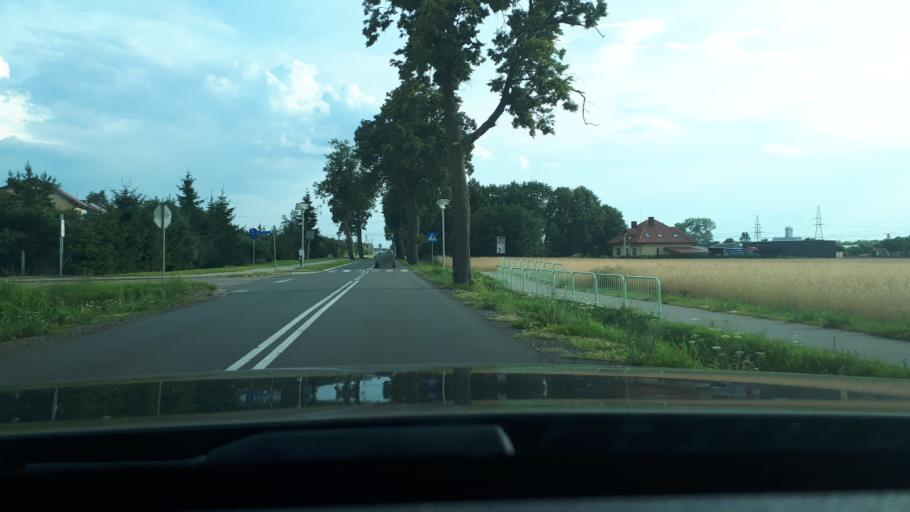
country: PL
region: Warmian-Masurian Voivodeship
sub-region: Powiat nidzicki
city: Nidzica
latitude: 53.3782
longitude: 20.4312
